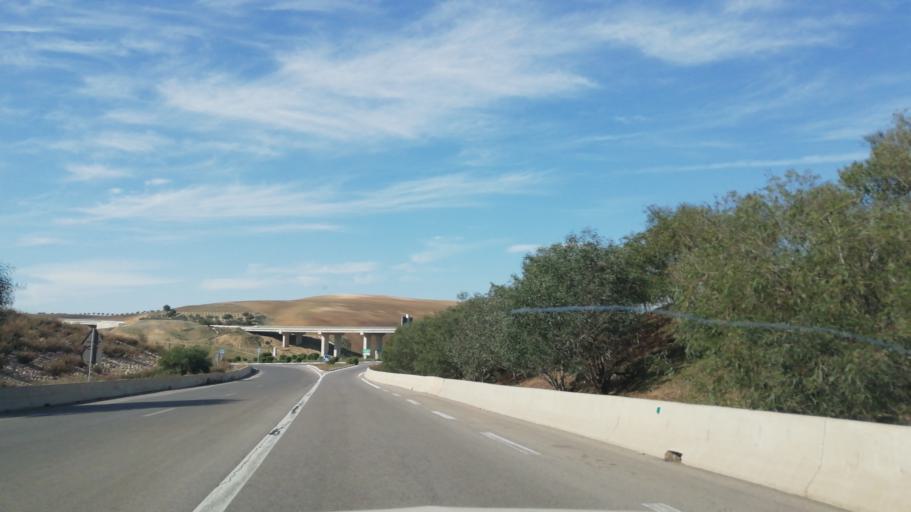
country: DZ
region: Tlemcen
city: Chetouane
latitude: 34.9802
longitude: -1.2360
